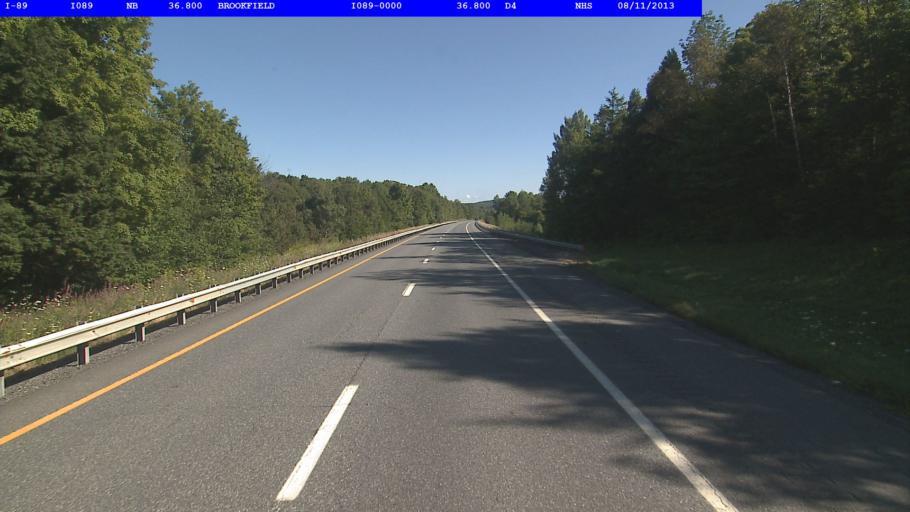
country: US
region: Vermont
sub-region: Orange County
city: Randolph
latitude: 44.0290
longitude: -72.6151
